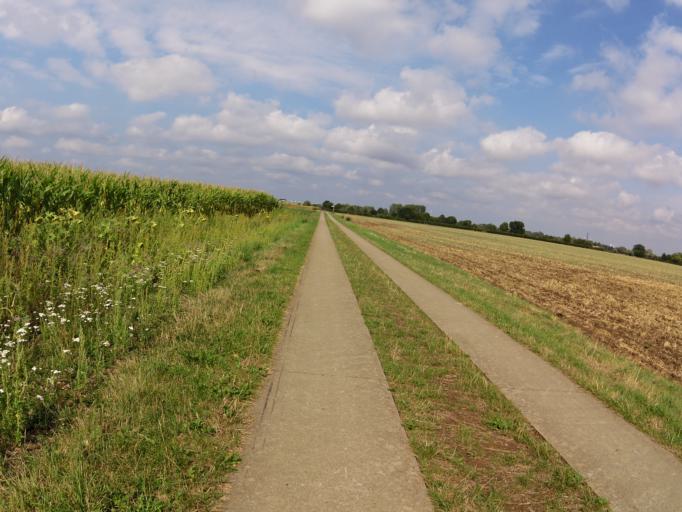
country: DE
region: Lower Saxony
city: Bucken
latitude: 52.7886
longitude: 9.1419
